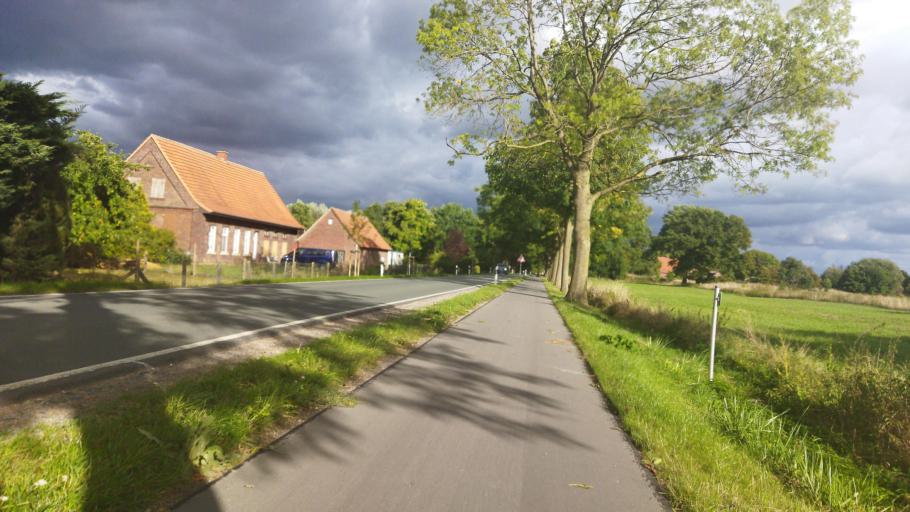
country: DE
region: North Rhine-Westphalia
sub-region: Regierungsbezirk Munster
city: Dulmen
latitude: 51.8950
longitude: 7.2586
